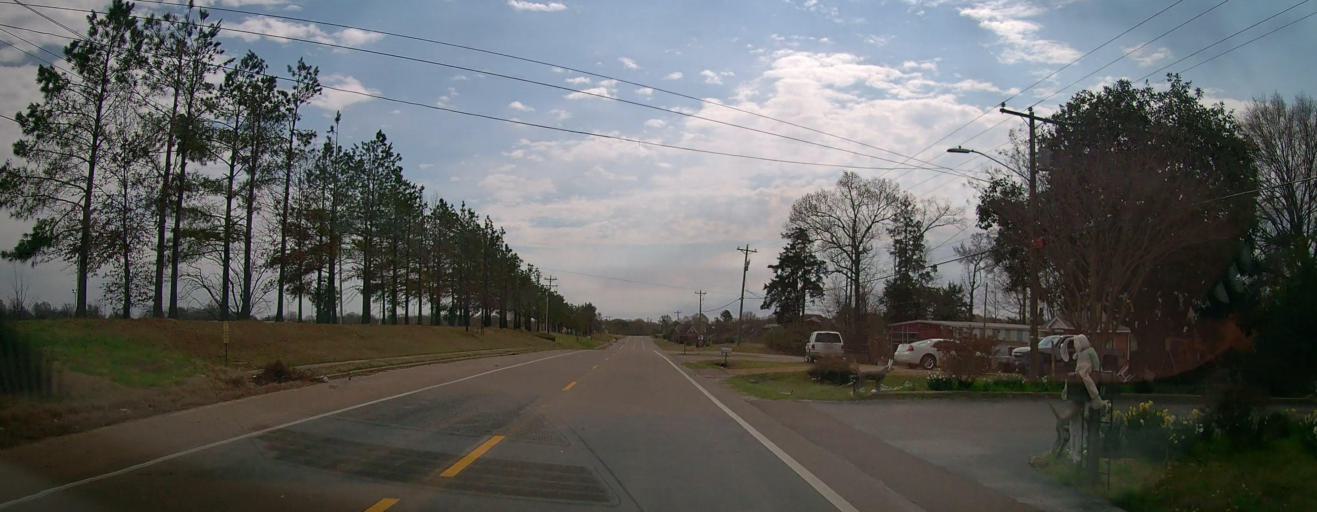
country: US
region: Mississippi
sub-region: De Soto County
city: Olive Branch
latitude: 34.9796
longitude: -89.8535
